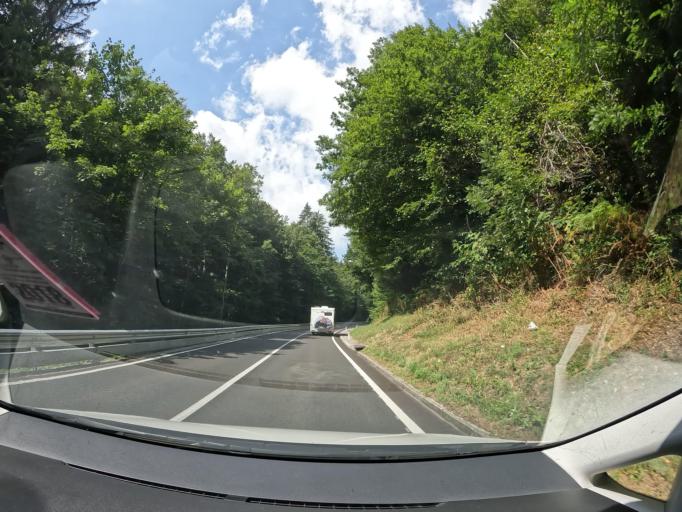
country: SI
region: Ilirska Bistrica
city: Ilirska Bistrica
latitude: 45.5220
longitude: 14.2496
